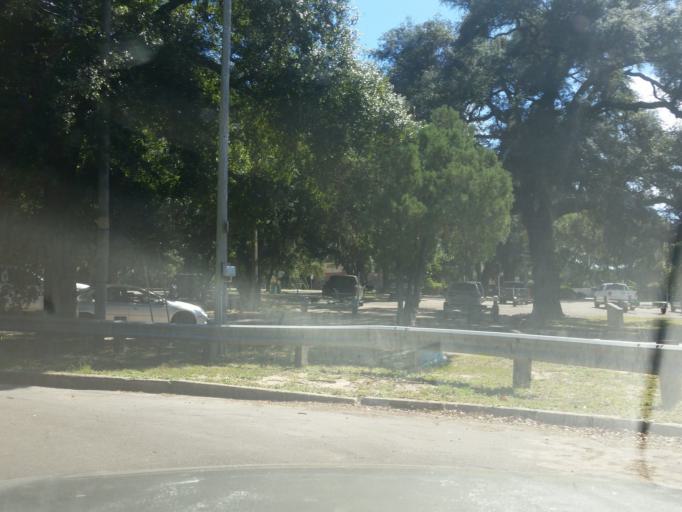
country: US
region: Florida
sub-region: Escambia County
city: East Pensacola Heights
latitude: 30.4266
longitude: -87.1860
